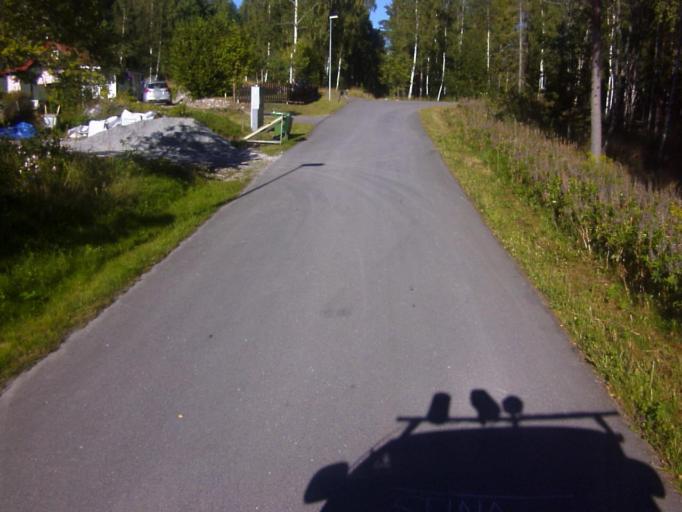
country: SE
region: Soedermanland
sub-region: Eskilstuna Kommun
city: Hallbybrunn
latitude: 59.3405
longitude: 16.4073
